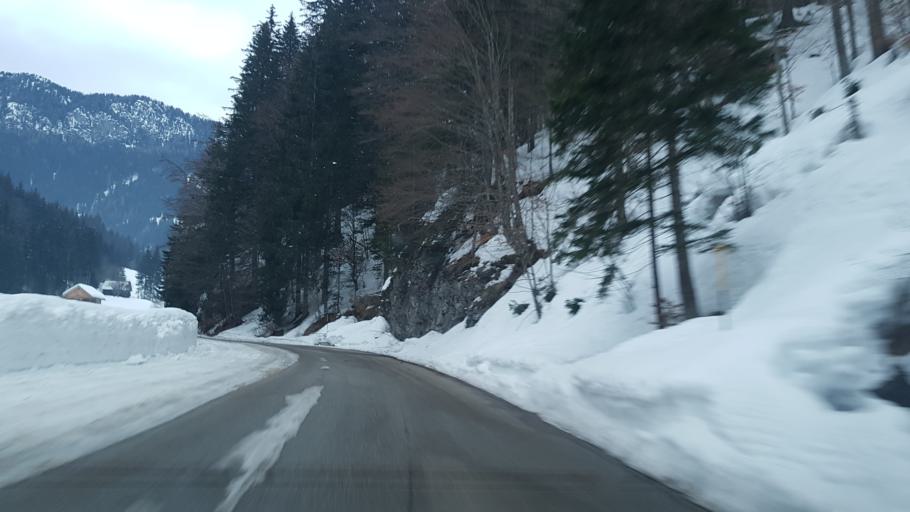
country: IT
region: Friuli Venezia Giulia
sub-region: Provincia di Udine
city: Malborghetto
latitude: 46.5386
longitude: 13.4741
